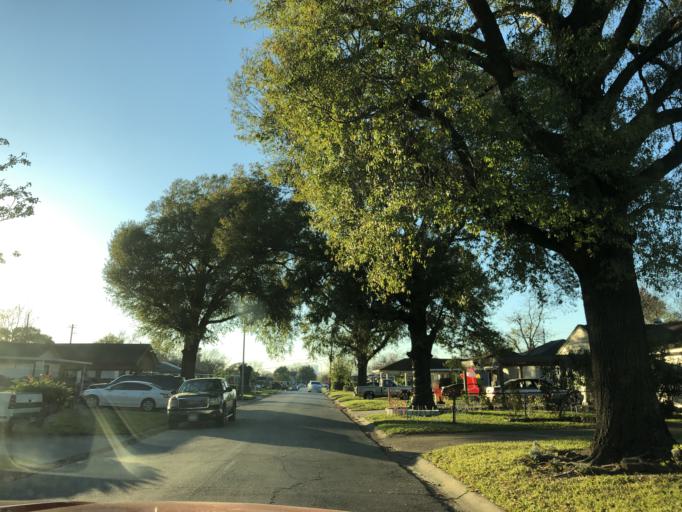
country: US
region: Texas
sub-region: Harris County
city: Jacinto City
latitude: 29.7611
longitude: -95.2686
